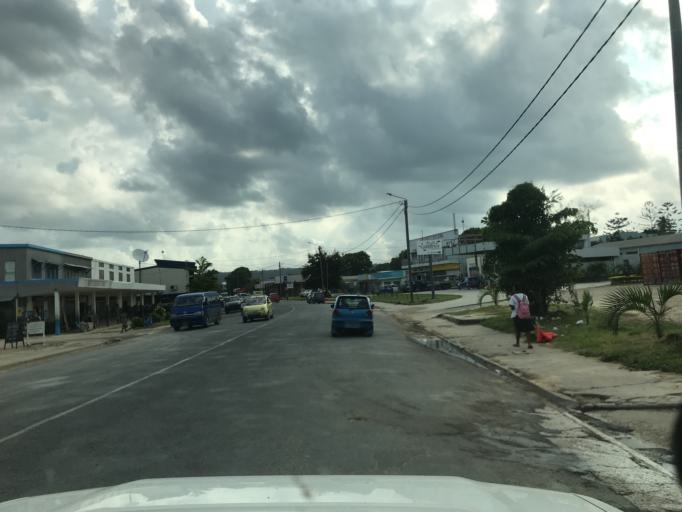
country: VU
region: Sanma
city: Luganville
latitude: -15.5135
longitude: 167.1811
